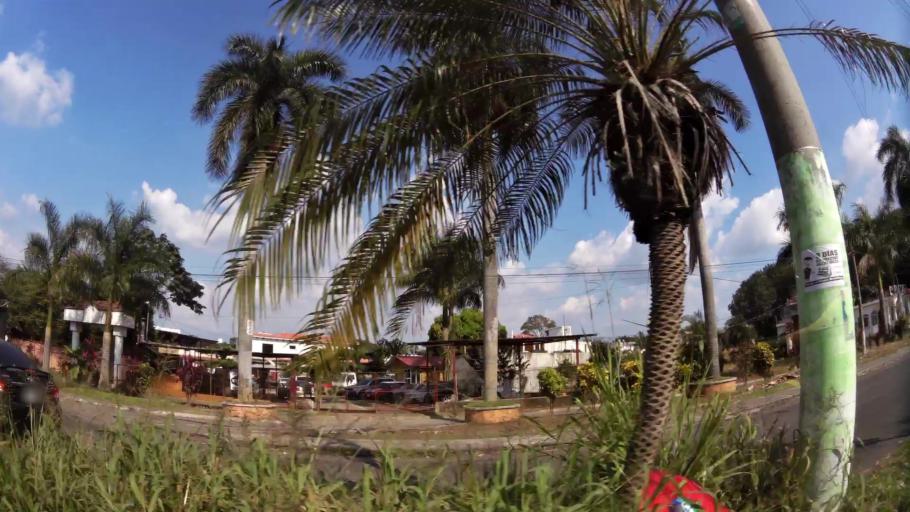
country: GT
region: Retalhuleu
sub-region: Municipio de Retalhuleu
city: Retalhuleu
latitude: 14.5449
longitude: -91.6782
